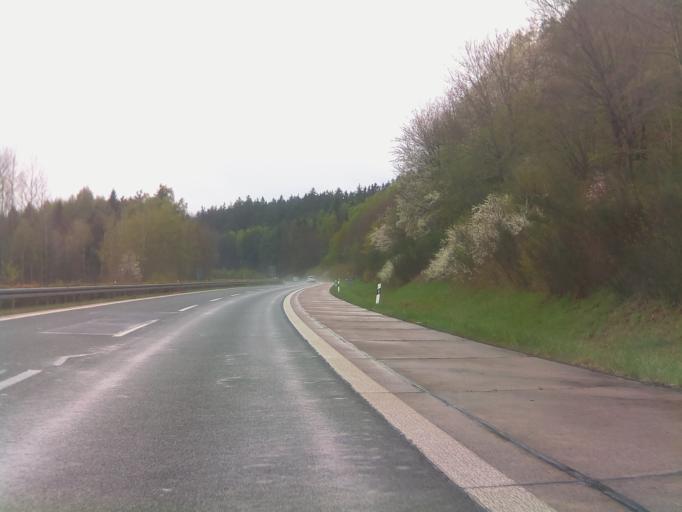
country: DE
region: Hesse
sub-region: Regierungsbezirk Kassel
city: Kirchheim
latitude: 50.8027
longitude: 9.5314
